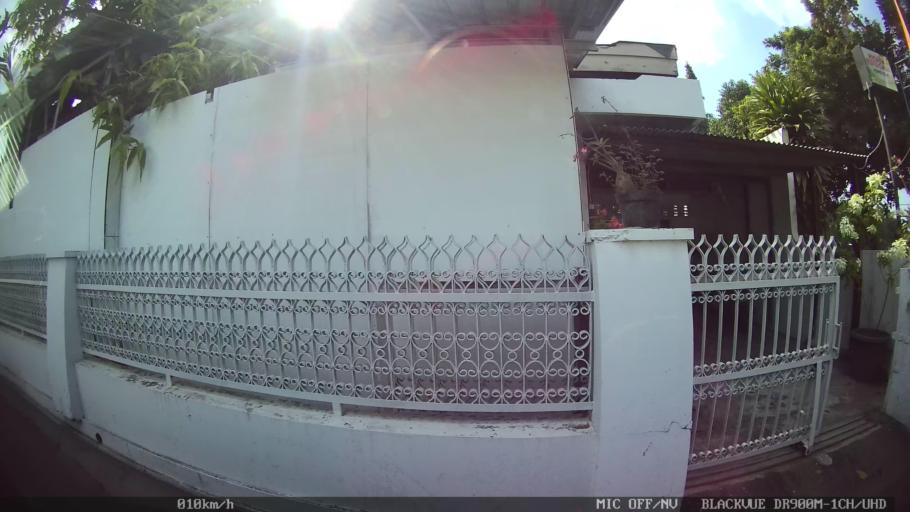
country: ID
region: Daerah Istimewa Yogyakarta
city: Kasihan
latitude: -7.8187
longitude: 110.3608
